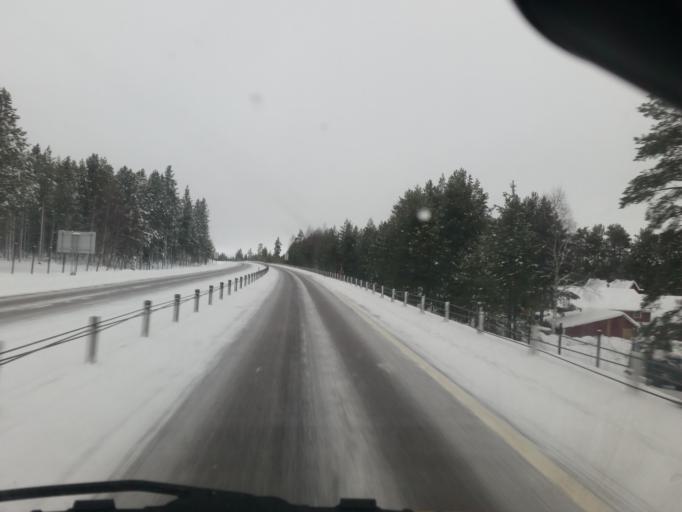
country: SE
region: Norrbotten
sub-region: Pitea Kommun
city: Pitea
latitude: 65.2144
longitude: 21.5210
